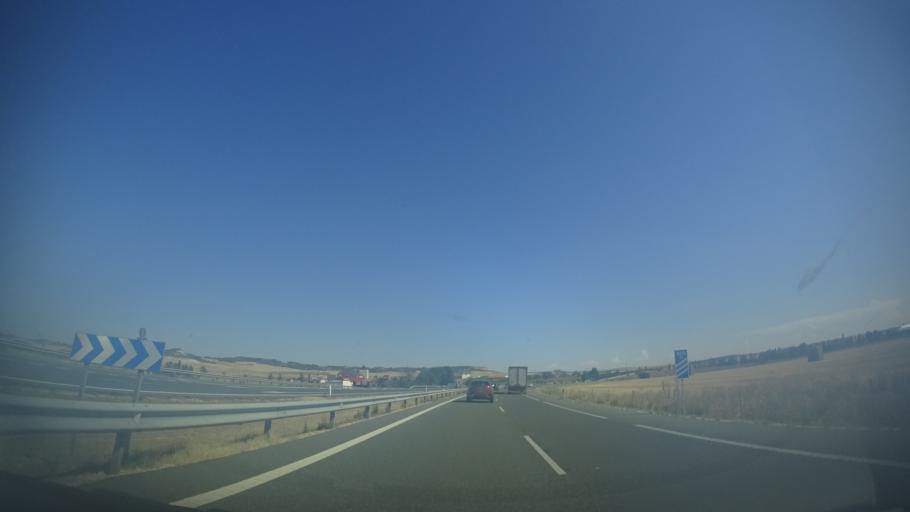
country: ES
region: Castille and Leon
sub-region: Provincia de Valladolid
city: Vega de Valdetronco
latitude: 41.5992
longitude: -5.1254
